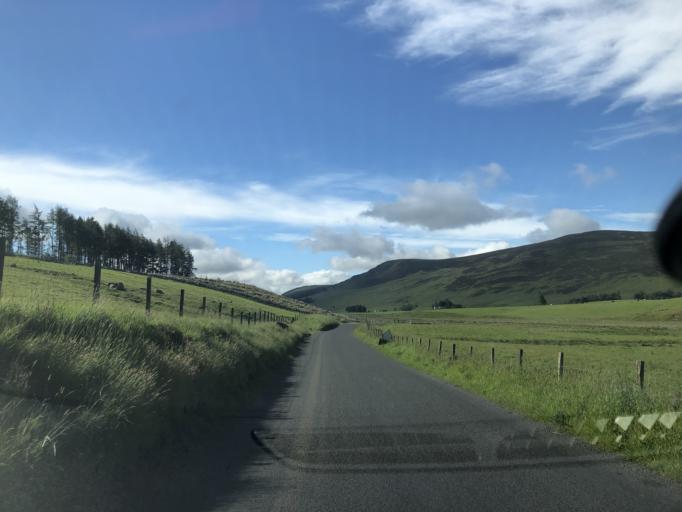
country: GB
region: Scotland
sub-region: Angus
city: Kirriemuir
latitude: 56.8031
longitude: -3.0374
